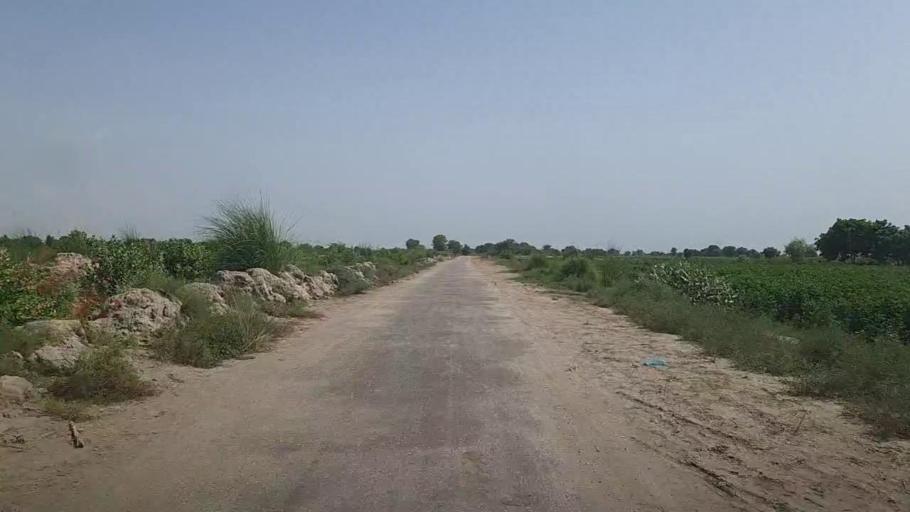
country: PK
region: Sindh
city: Pad Idan
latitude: 26.8328
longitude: 68.3306
